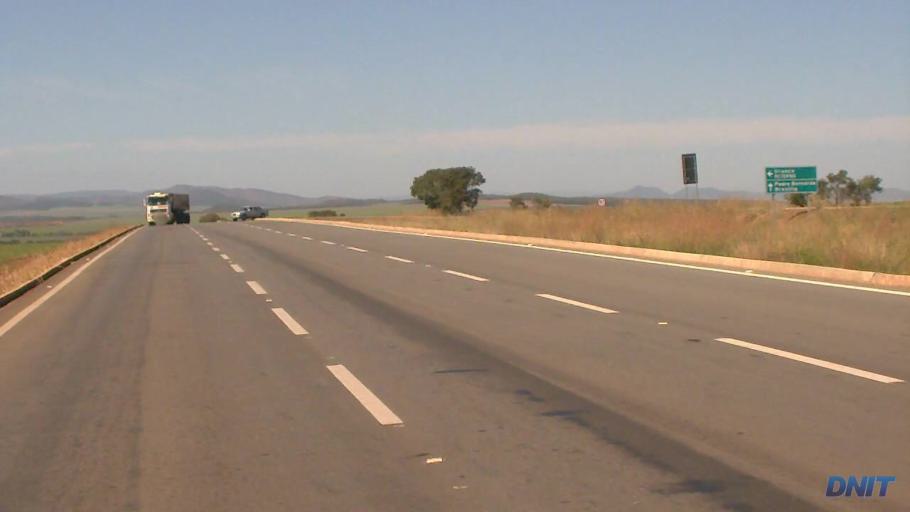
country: BR
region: Goias
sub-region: Barro Alto
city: Barro Alto
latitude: -15.0238
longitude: -48.8959
